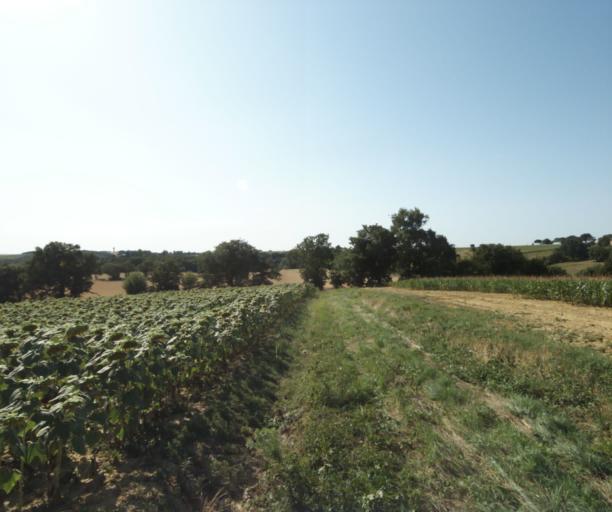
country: FR
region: Midi-Pyrenees
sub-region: Departement de la Haute-Garonne
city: Avignonet-Lauragais
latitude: 43.4264
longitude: 1.8021
